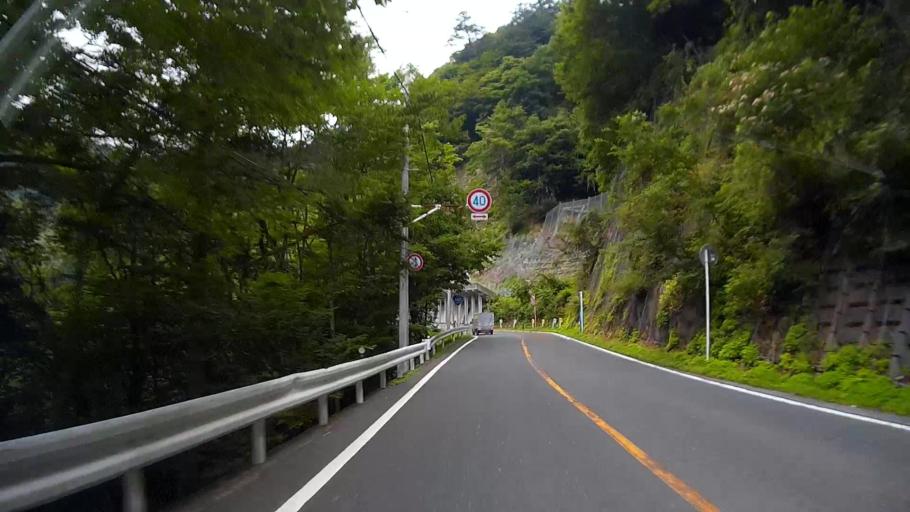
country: JP
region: Yamanashi
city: Enzan
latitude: 35.9134
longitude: 138.8229
